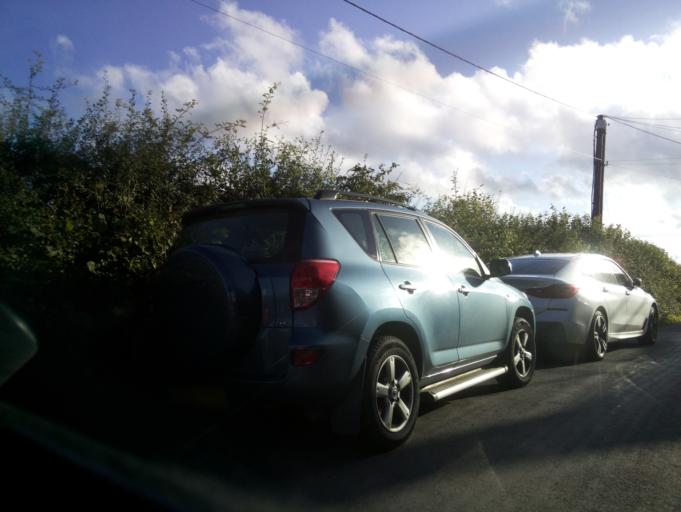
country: GB
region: England
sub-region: Devon
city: Totnes
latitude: 50.3457
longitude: -3.6832
